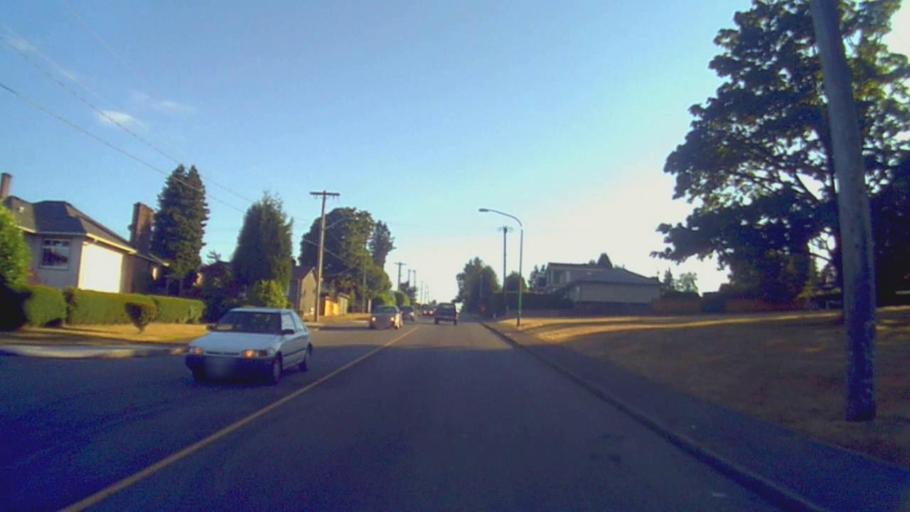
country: CA
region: British Columbia
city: New Westminster
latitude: 49.2325
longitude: -122.9022
